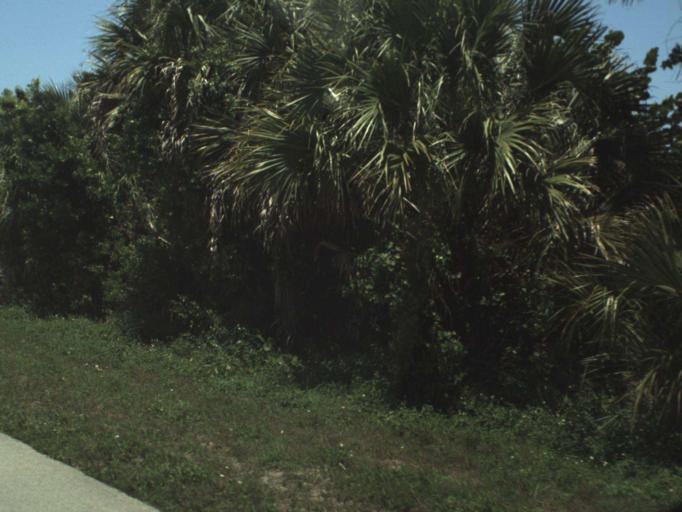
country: US
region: Florida
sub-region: Brevard County
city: Micco
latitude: 27.8735
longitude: -80.4553
